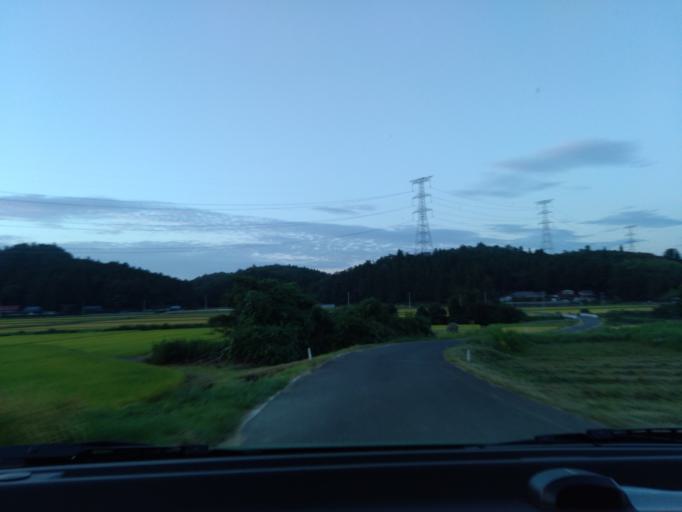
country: JP
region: Iwate
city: Ichinoseki
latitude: 38.8585
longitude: 141.1437
